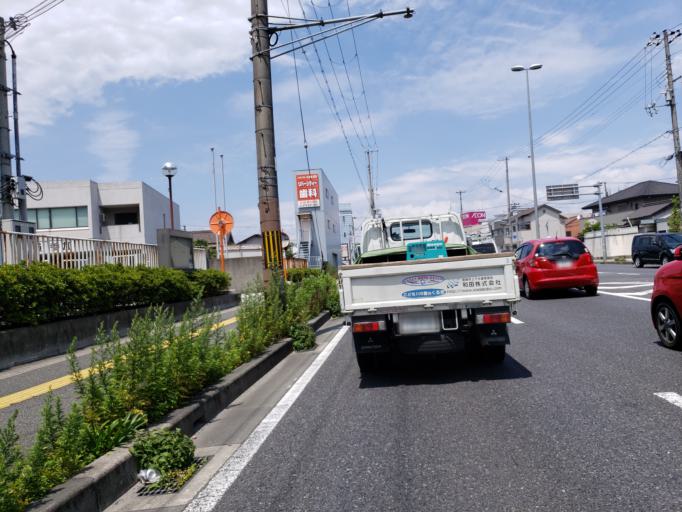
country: JP
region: Hyogo
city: Himeji
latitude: 34.7958
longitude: 134.6711
